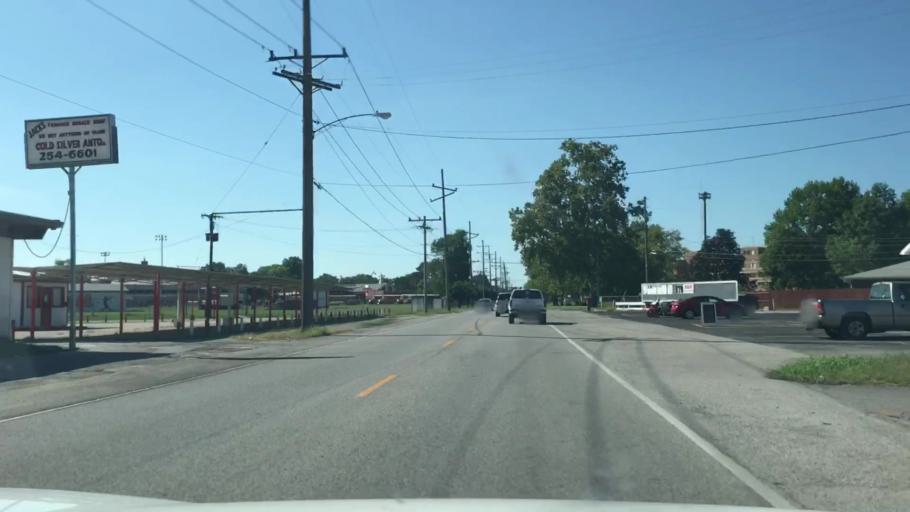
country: US
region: Illinois
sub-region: Madison County
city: Wood River
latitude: 38.8710
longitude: -90.0932
